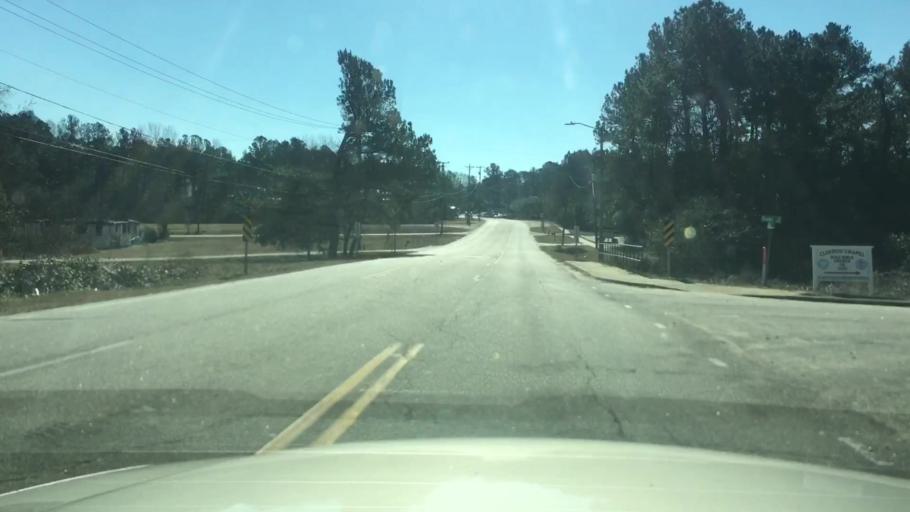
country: US
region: North Carolina
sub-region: Cumberland County
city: Fayetteville
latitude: 35.0405
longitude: -78.8973
